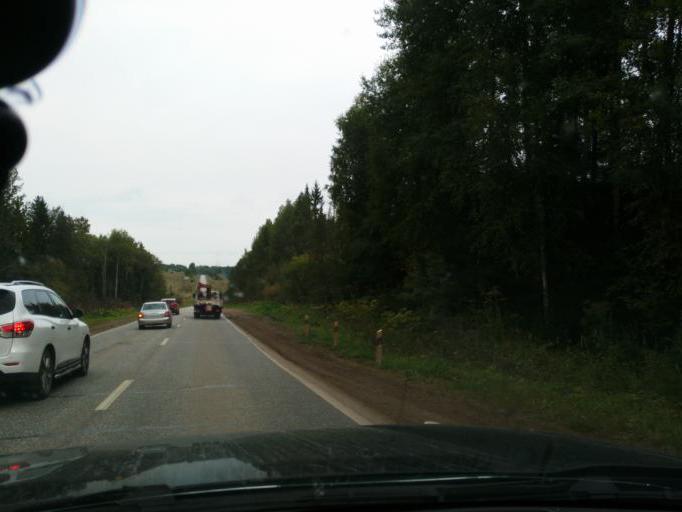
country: RU
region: Perm
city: Chernushka
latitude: 56.5701
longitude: 56.1249
